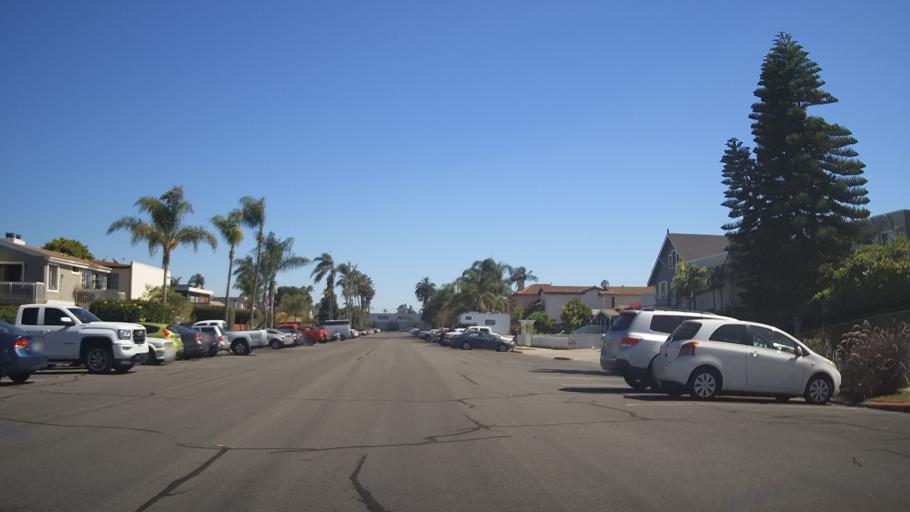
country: US
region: California
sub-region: San Diego County
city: San Diego
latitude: 32.7607
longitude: -117.1476
